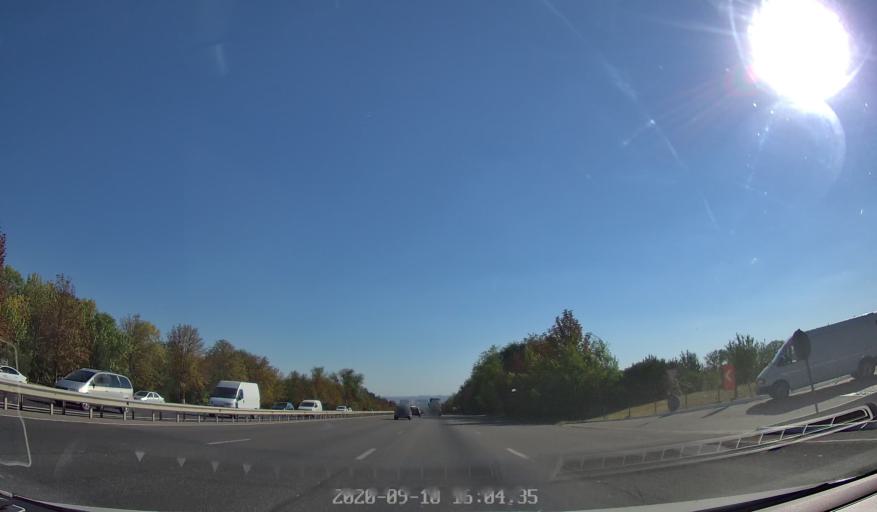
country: MD
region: Chisinau
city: Stauceni
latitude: 47.0907
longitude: 28.8621
